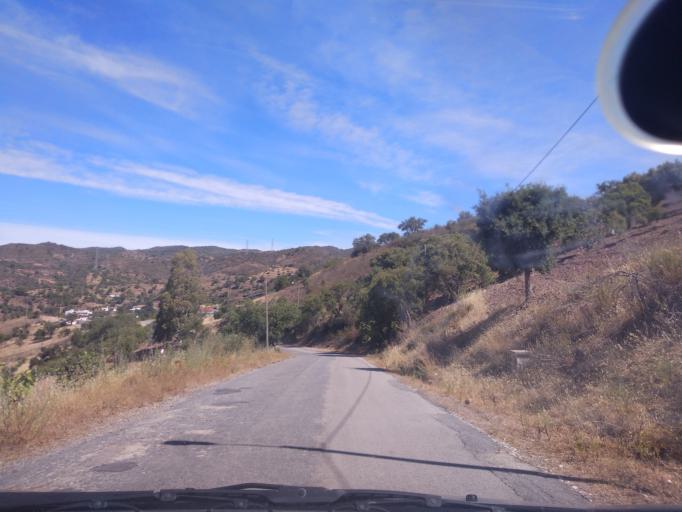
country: PT
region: Faro
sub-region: Sao Bras de Alportel
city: Sao Bras de Alportel
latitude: 37.1746
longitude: -7.8061
